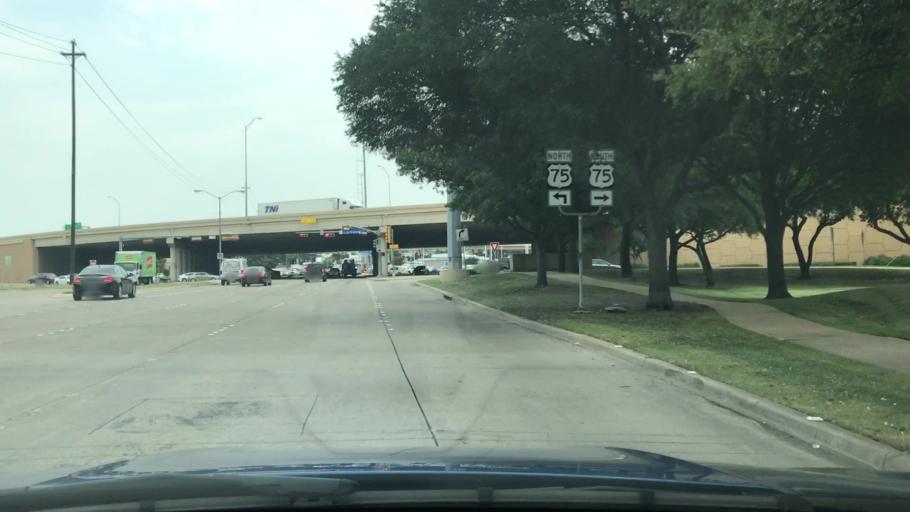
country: US
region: Texas
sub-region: Dallas County
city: Richardson
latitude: 32.9607
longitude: -96.7294
